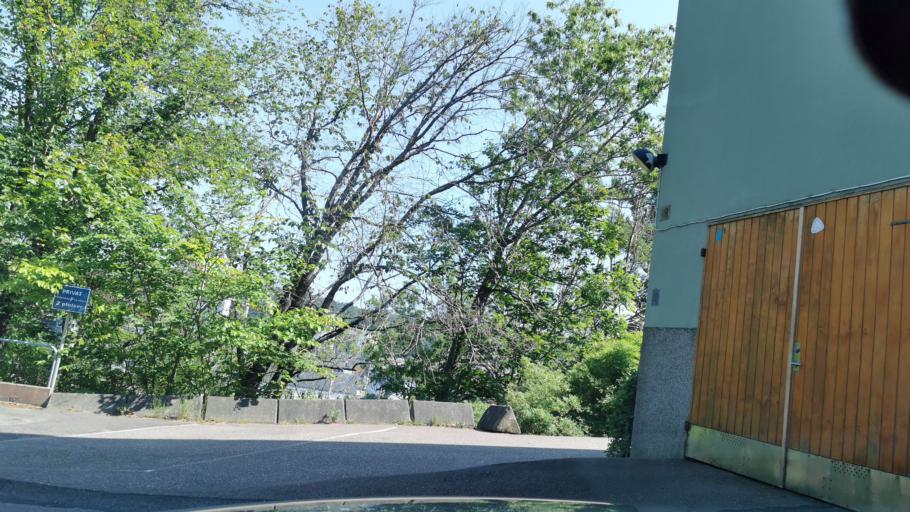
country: SE
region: Vaestra Goetaland
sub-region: Molndal
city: Moelndal
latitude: 57.6795
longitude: 11.9976
